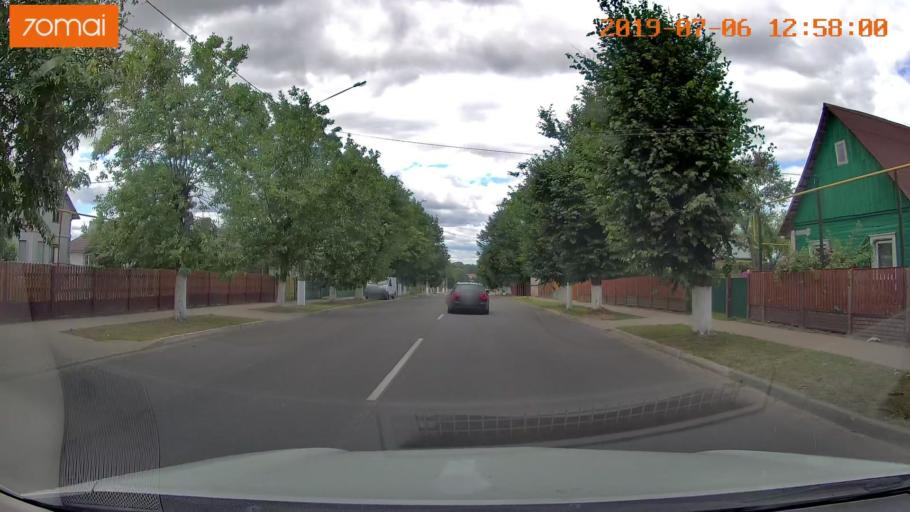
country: BY
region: Minsk
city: Dzyarzhynsk
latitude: 53.6867
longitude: 27.1474
